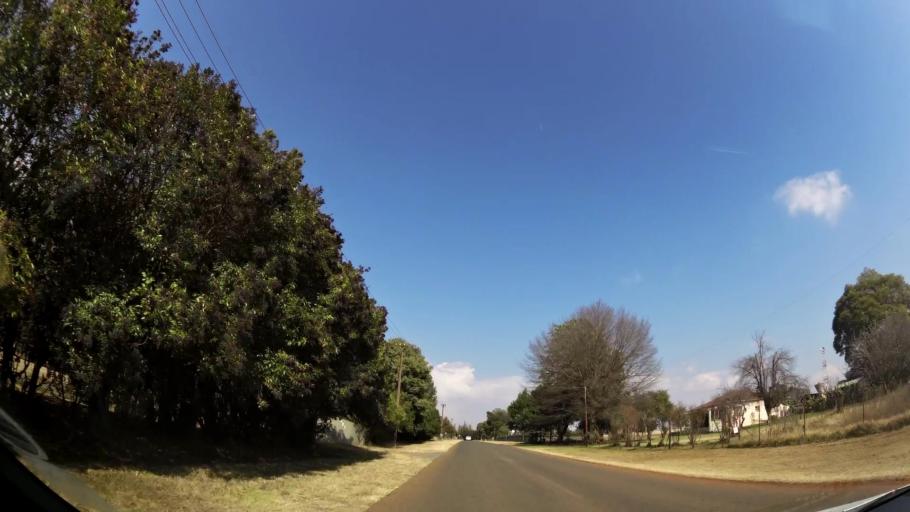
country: ZA
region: Mpumalanga
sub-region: Nkangala District Municipality
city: Delmas
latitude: -26.1698
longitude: 28.5387
